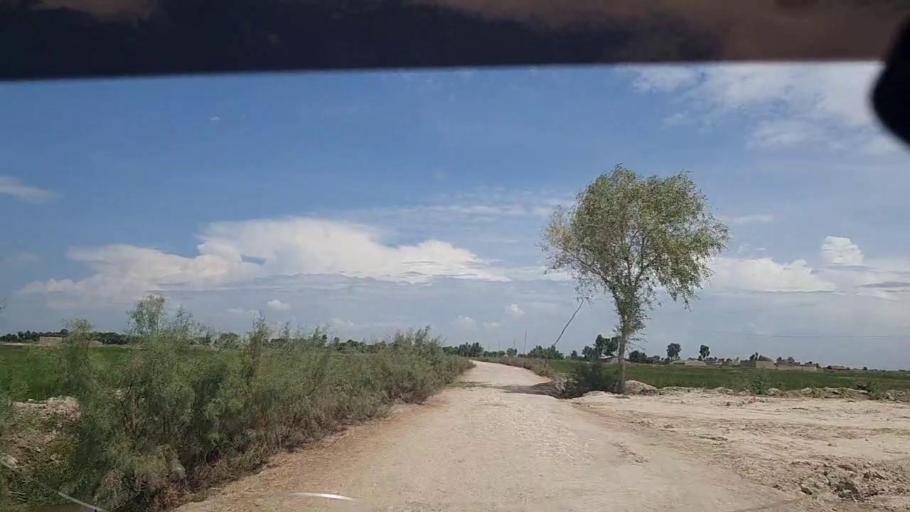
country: PK
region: Sindh
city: Ghauspur
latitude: 28.1507
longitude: 68.9482
